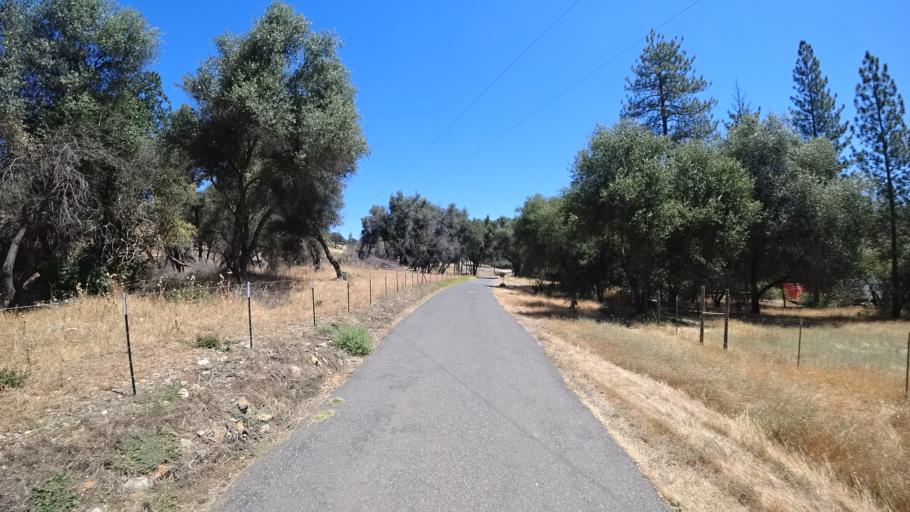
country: US
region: California
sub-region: Calaveras County
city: Mountain Ranch
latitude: 38.1845
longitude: -120.5758
